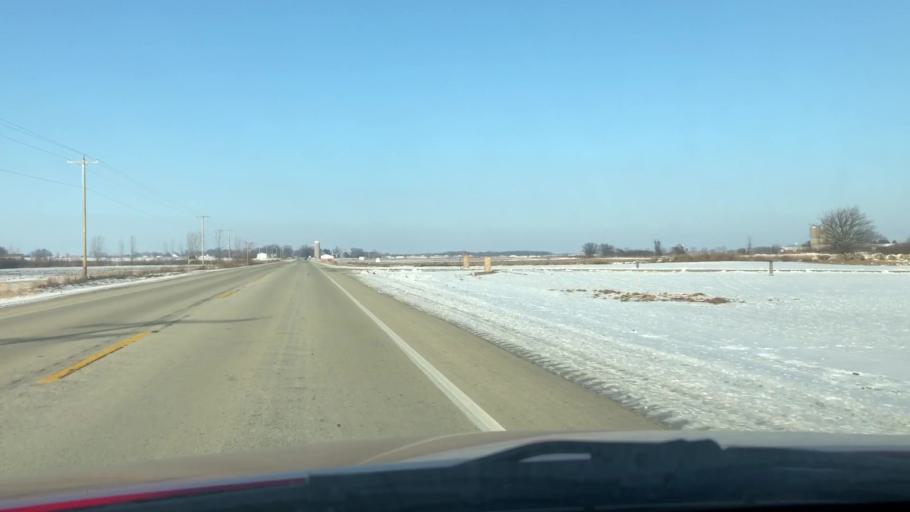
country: US
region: Wisconsin
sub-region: Outagamie County
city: Seymour
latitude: 44.4807
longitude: -88.3295
